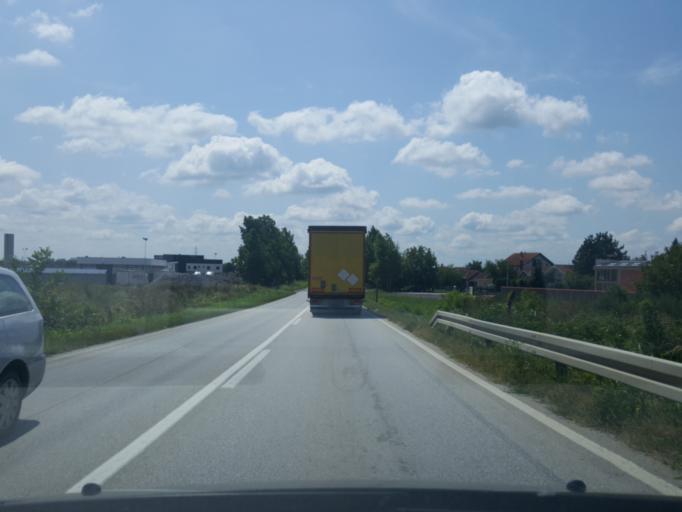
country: RS
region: Autonomna Pokrajina Vojvodina
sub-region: Sremski Okrug
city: Sremska Mitrovica
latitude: 44.9824
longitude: 19.6392
